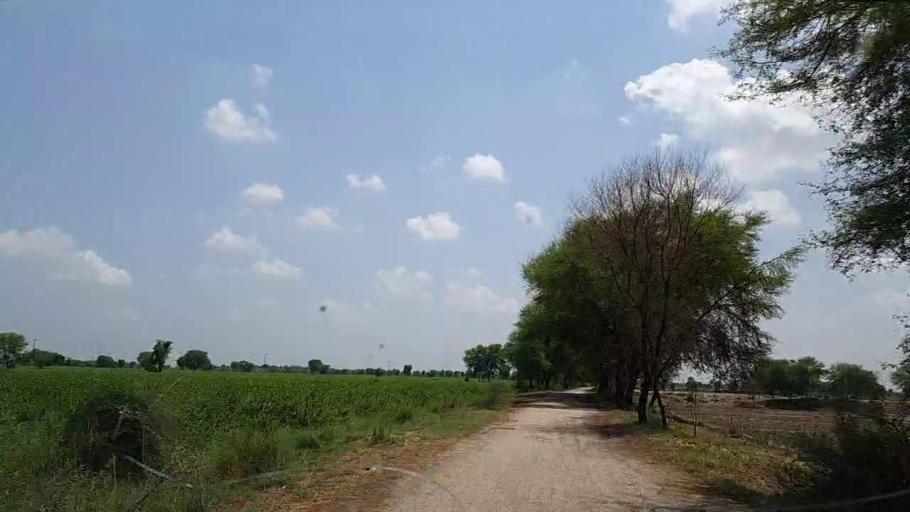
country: PK
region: Sindh
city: Tharu Shah
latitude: 27.0131
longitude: 68.0683
